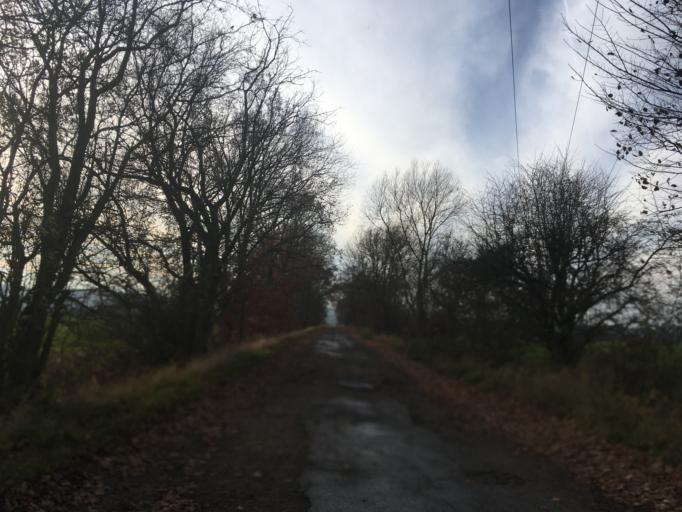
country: DE
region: Brandenburg
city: Falkenberg
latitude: 52.8195
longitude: 13.9966
